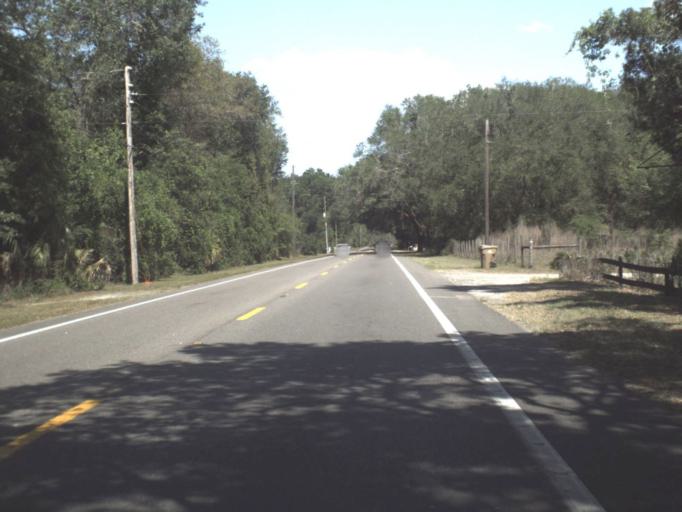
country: US
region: Florida
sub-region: Lake County
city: Mount Plymouth
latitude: 28.8184
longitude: -81.4817
